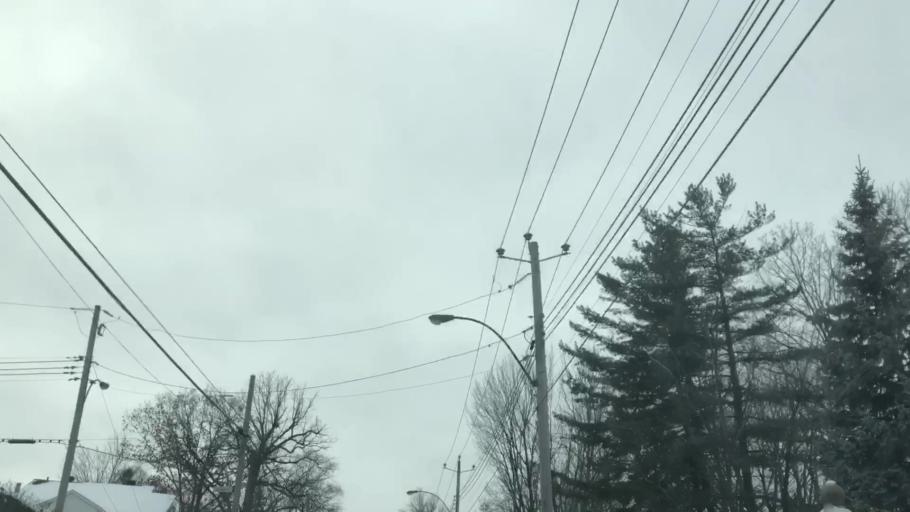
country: CA
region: Quebec
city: Dorval
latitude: 45.5119
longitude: -73.7510
